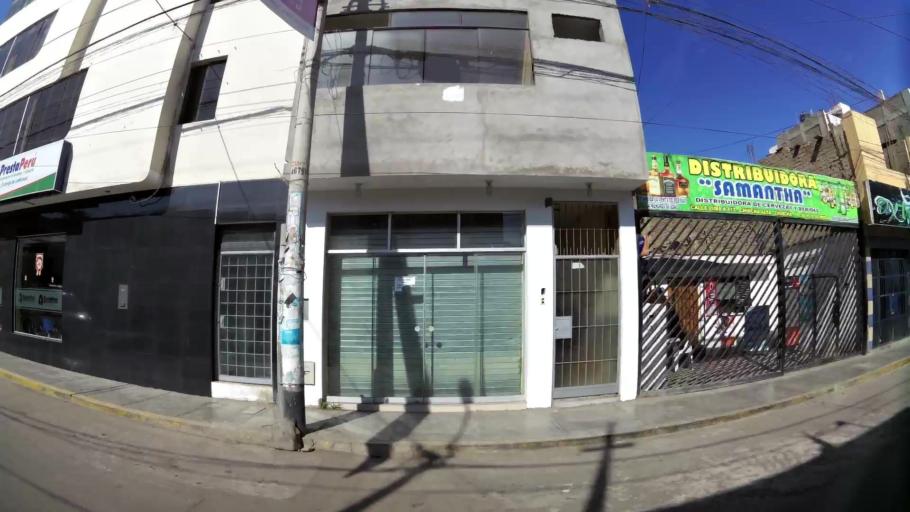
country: PE
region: Ica
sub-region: Provincia de Chincha
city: Chincha Alta
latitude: -13.4197
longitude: -76.1337
